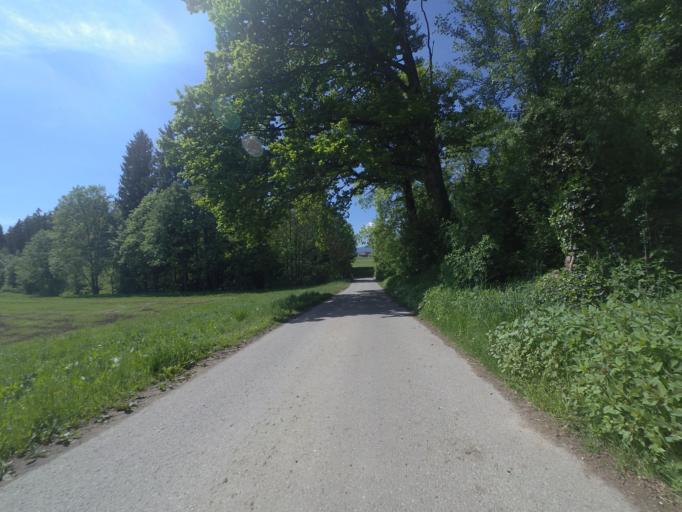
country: DE
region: Bavaria
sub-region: Upper Bavaria
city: Petting
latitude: 47.8878
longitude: 12.8351
